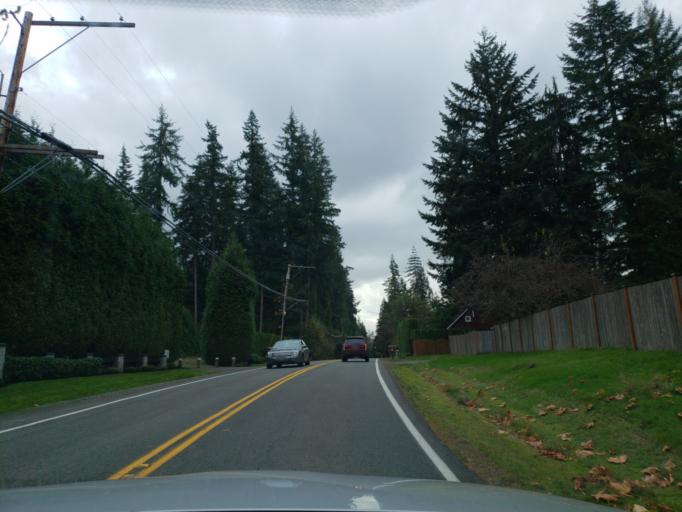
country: US
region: Washington
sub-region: King County
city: Woodinville
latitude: 47.7465
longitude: -122.1288
